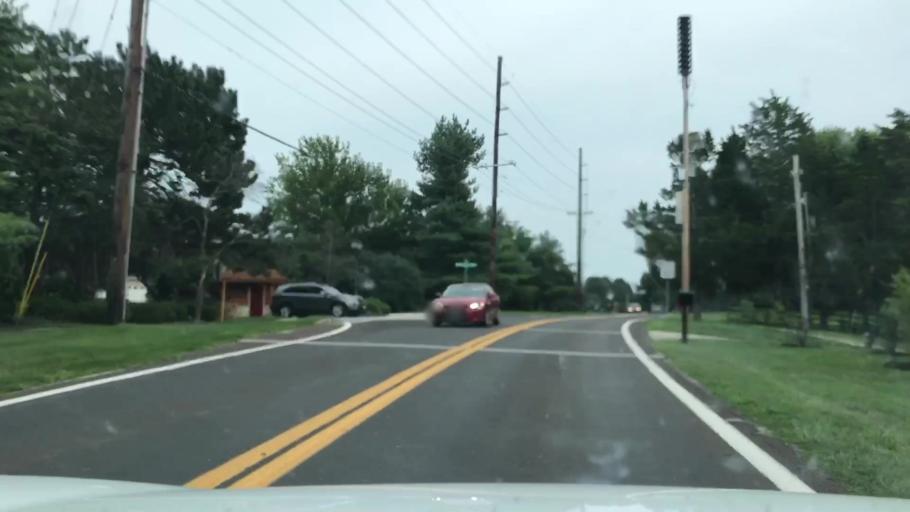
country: US
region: Missouri
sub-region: Saint Louis County
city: Clarkson Valley
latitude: 38.6313
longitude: -90.5998
